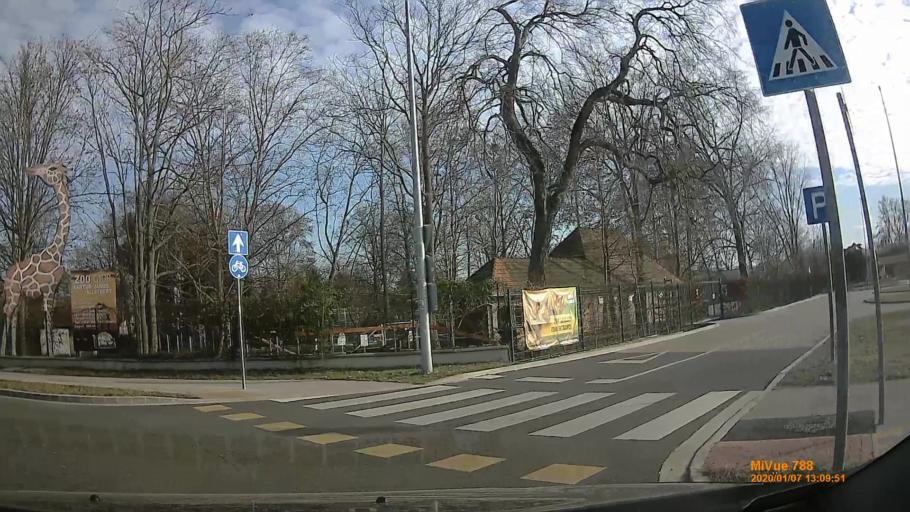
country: HU
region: Gyor-Moson-Sopron
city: Gyor
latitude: 47.6952
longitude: 17.6671
